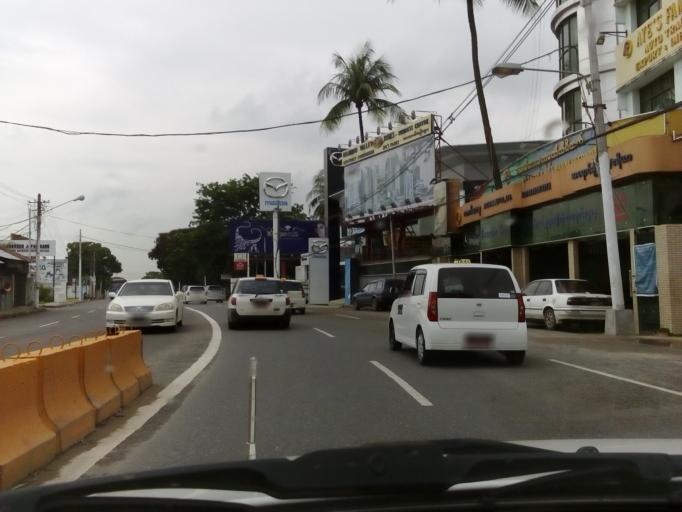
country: MM
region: Yangon
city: Yangon
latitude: 16.8186
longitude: 96.1565
